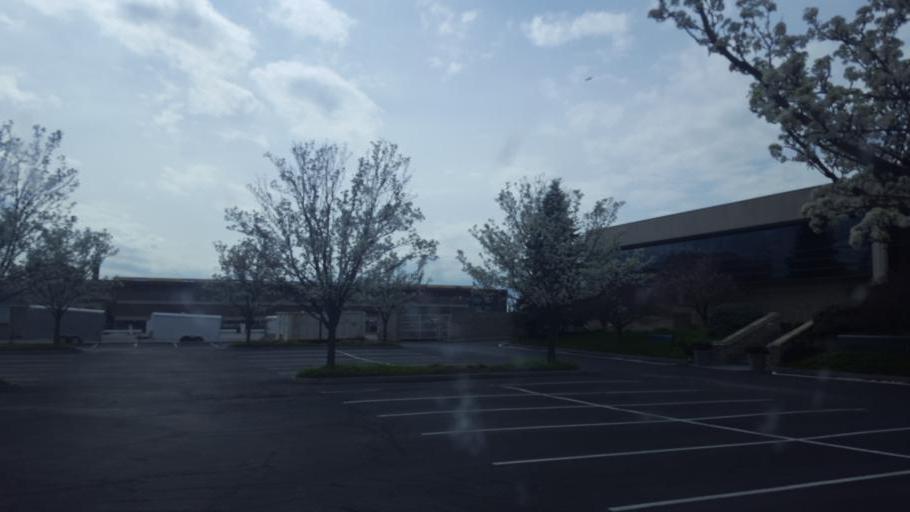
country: US
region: Ohio
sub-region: Erie County
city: Sandusky
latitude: 41.4584
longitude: -82.7114
